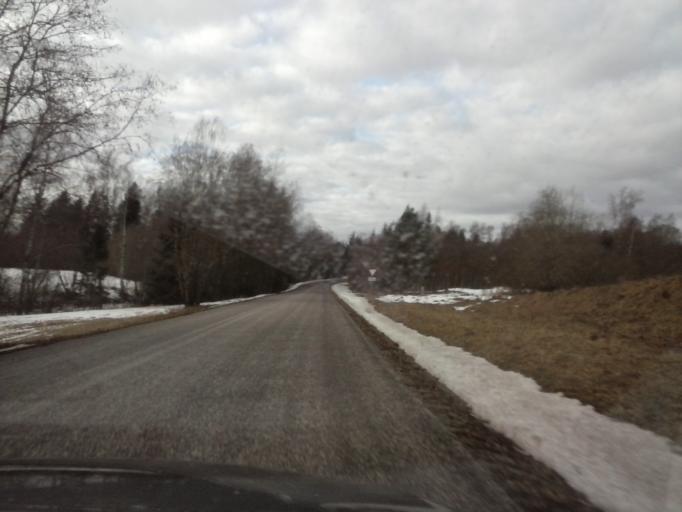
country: EE
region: Tartu
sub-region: Elva linn
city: Elva
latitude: 58.0001
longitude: 26.2720
